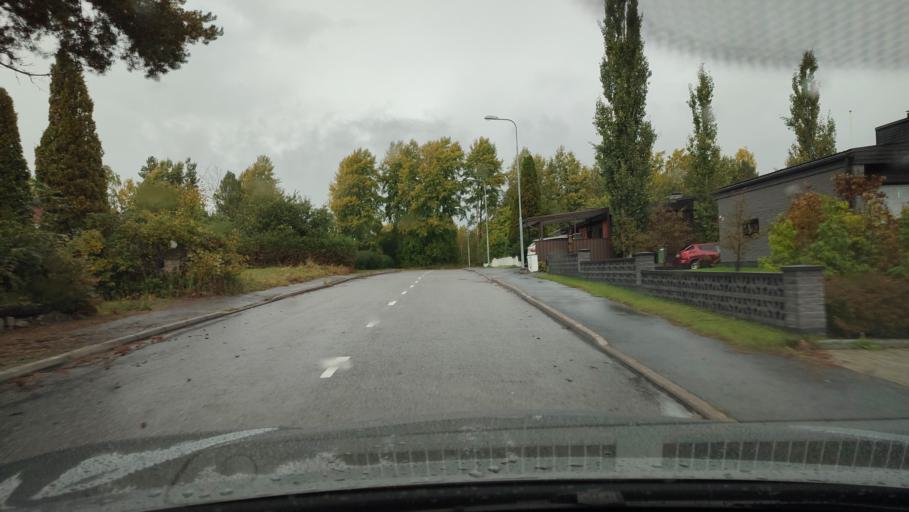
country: FI
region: Ostrobothnia
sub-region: Sydosterbotten
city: Kristinestad
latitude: 62.2832
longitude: 21.3765
